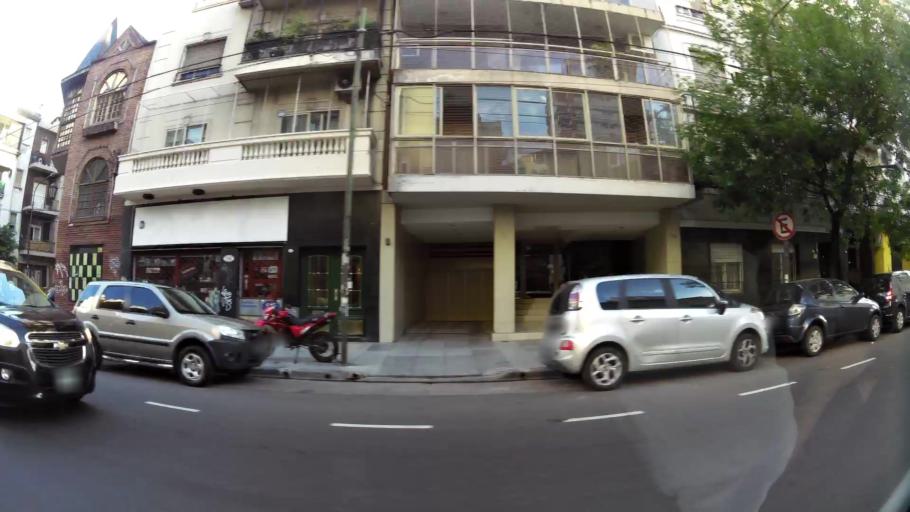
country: AR
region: Buenos Aires F.D.
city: Colegiales
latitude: -34.6032
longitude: -58.4343
